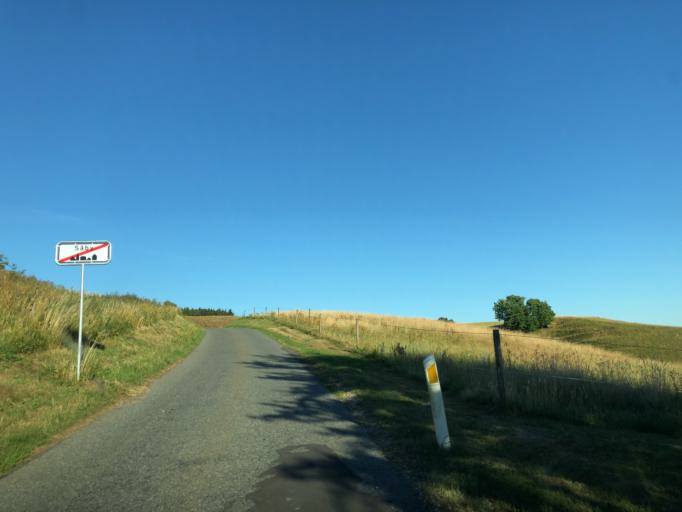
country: DK
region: Central Jutland
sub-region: Skanderborg Kommune
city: Ry
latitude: 55.9860
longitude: 9.7900
